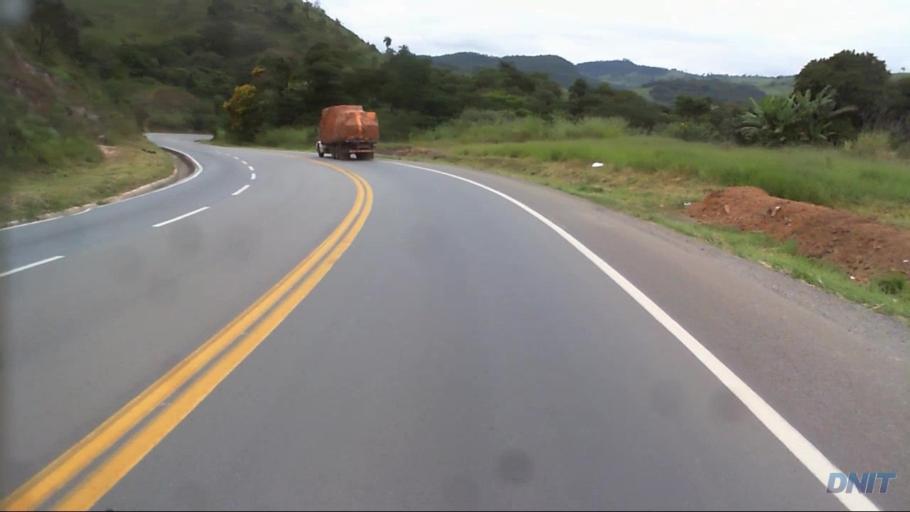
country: BR
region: Minas Gerais
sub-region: Joao Monlevade
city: Joao Monlevade
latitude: -19.8573
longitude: -43.2268
